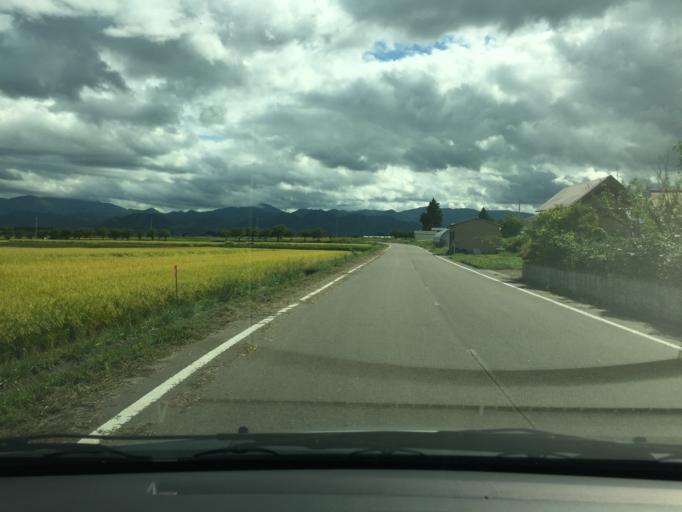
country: JP
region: Fukushima
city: Kitakata
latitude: 37.4778
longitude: 139.8192
